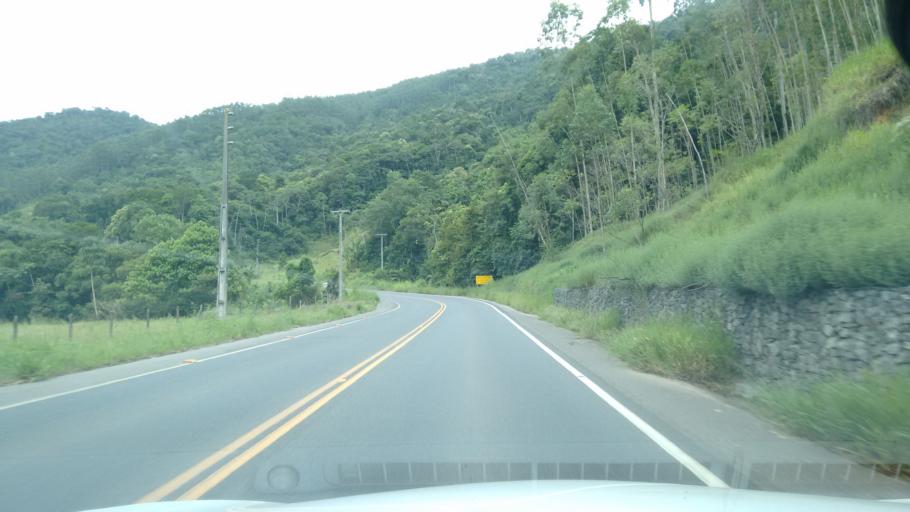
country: BR
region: Santa Catarina
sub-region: Pomerode
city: Pomerode
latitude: -26.7588
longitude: -49.2317
